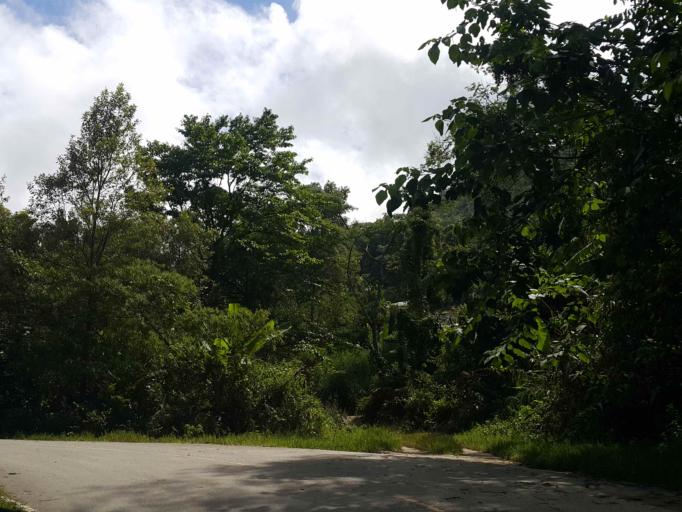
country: TH
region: Chiang Mai
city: Mae Chaem
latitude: 18.5211
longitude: 98.5218
